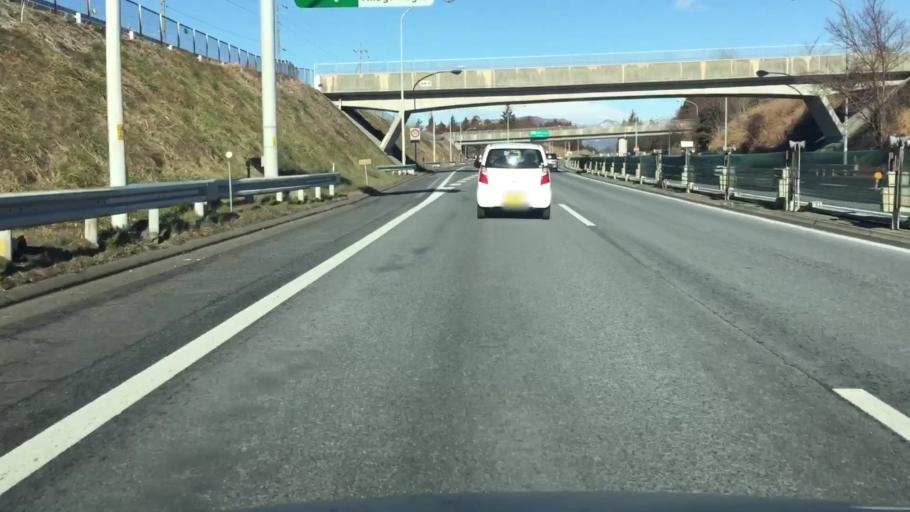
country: JP
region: Gunma
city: Numata
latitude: 36.5988
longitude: 139.0636
